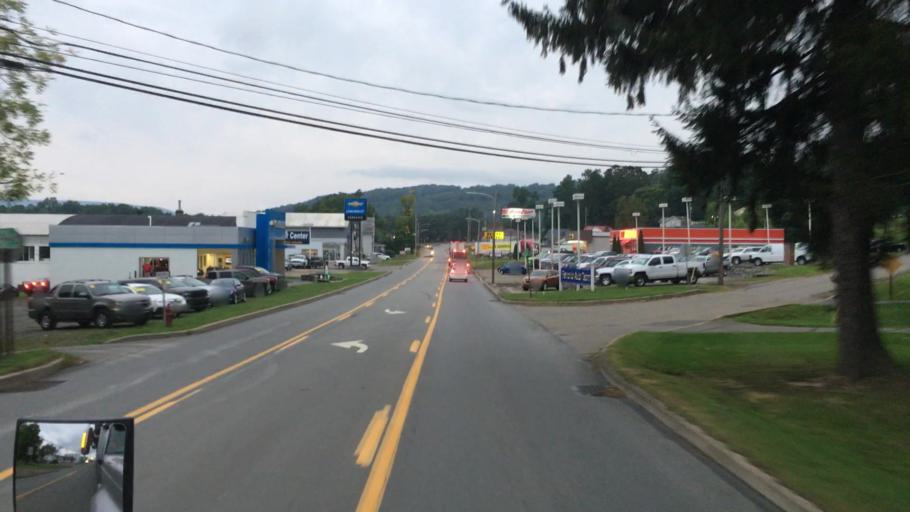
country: US
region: Pennsylvania
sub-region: Bradford County
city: Towanda
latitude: 41.7654
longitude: -76.4304
